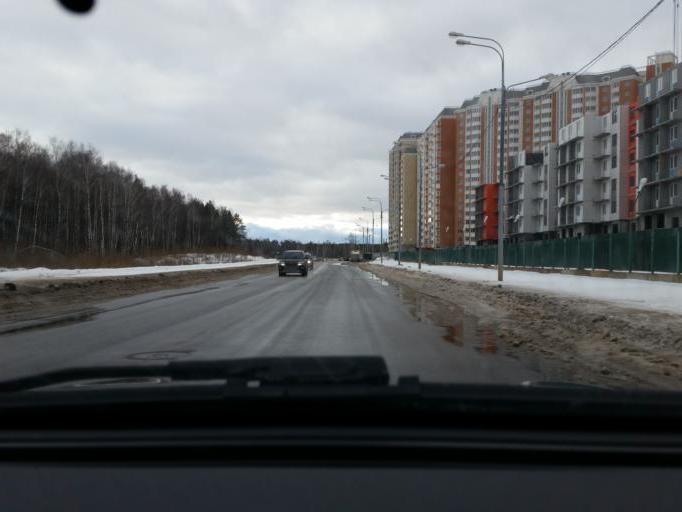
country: RU
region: Moskovskaya
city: Shcherbinka
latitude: 55.5243
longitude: 37.5999
